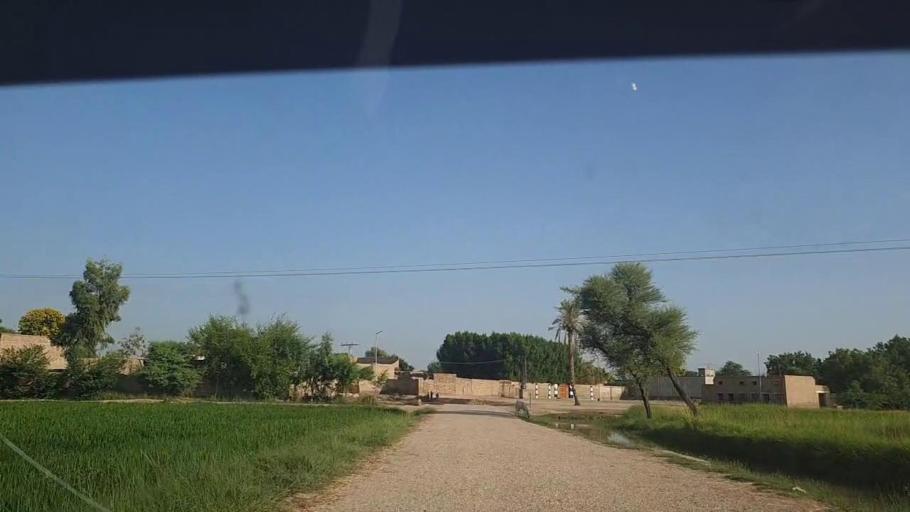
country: PK
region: Sindh
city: Tangwani
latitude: 28.2651
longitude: 69.0140
